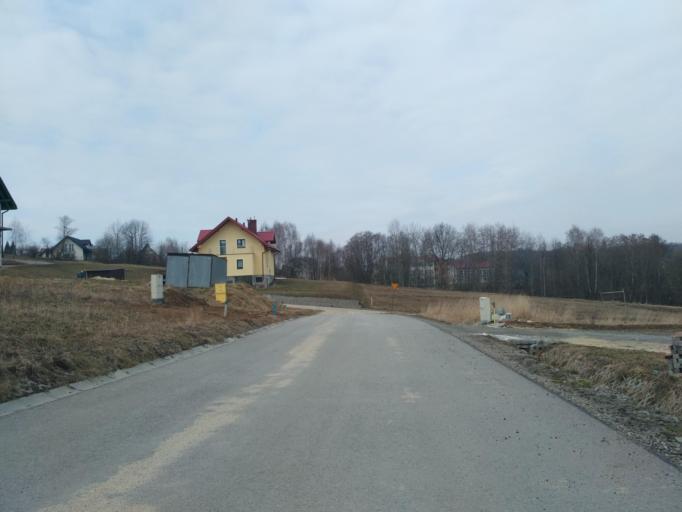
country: PL
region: Subcarpathian Voivodeship
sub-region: Powiat ropczycko-sedziszowski
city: Wielopole Skrzynskie
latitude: 49.9416
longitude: 21.6128
